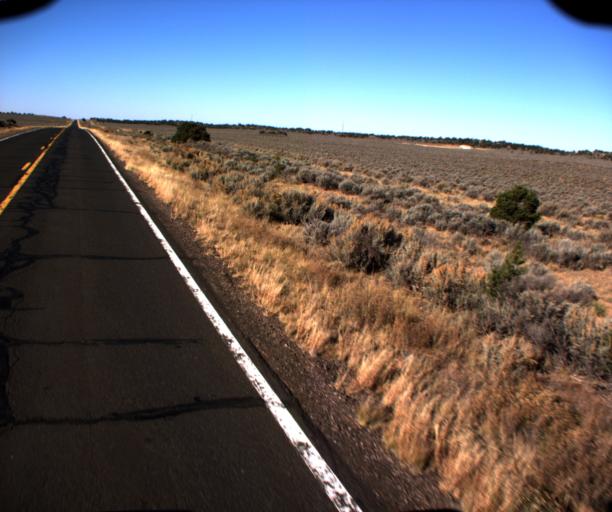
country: US
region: Arizona
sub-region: Navajo County
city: First Mesa
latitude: 35.7461
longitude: -110.0565
